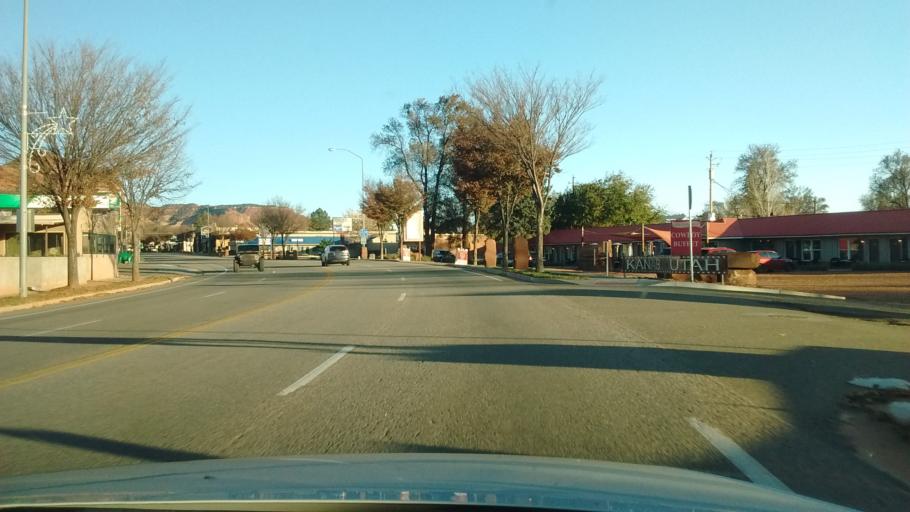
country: US
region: Utah
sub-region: Kane County
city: Kanab
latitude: 37.0483
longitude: -112.5340
